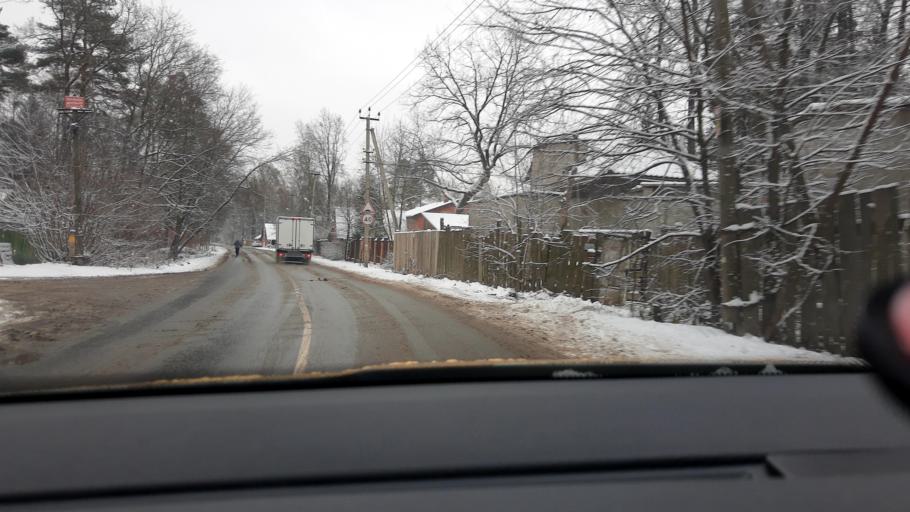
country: RU
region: Moskovskaya
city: Mamontovka
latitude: 55.9696
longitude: 37.8283
